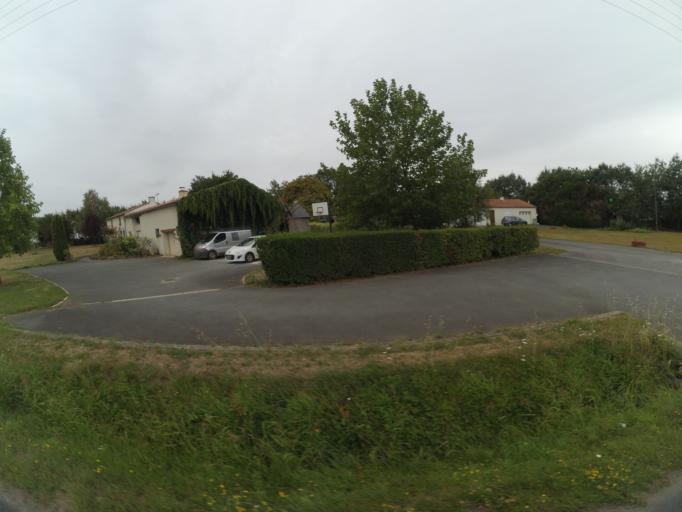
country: FR
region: Pays de la Loire
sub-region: Departement de la Vendee
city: Saint-Andre-Treize-Voies
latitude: 46.9188
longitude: -1.3893
